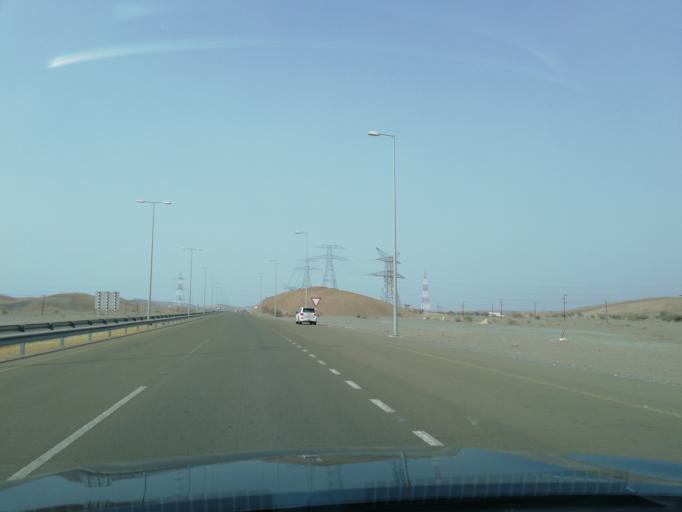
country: OM
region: Al Batinah
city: Al Liwa'
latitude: 24.3512
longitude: 56.5216
